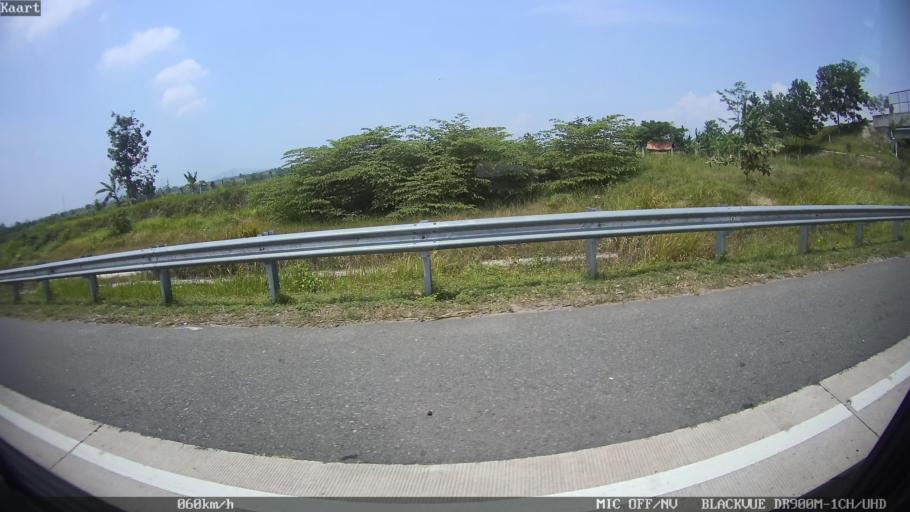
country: ID
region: Lampung
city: Kedaton
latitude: -5.3411
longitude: 105.3112
